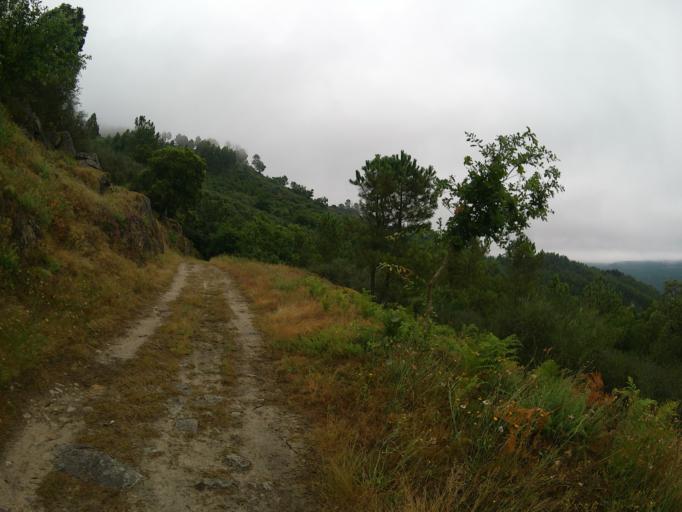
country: PT
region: Viana do Castelo
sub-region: Ponte de Lima
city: Ponte de Lima
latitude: 41.7229
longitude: -8.6097
